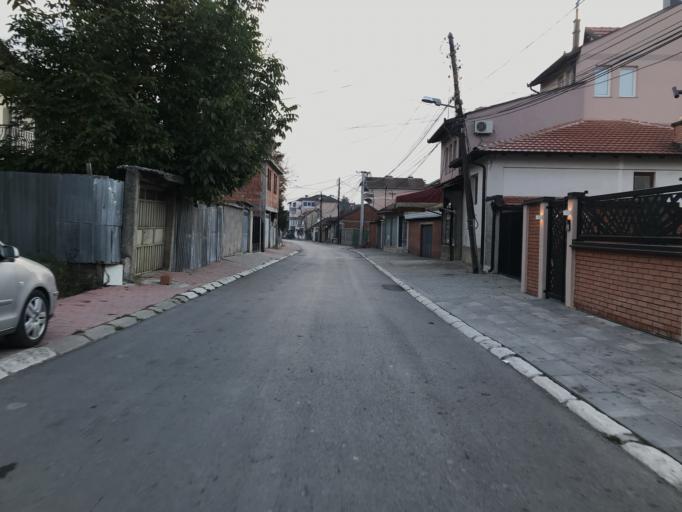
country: XK
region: Pec
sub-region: Komuna e Pejes
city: Peje
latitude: 42.6597
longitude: 20.2993
